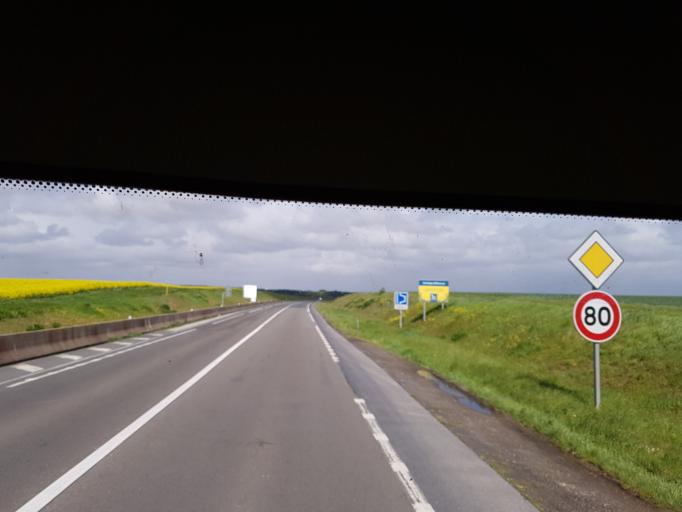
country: FR
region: Nord-Pas-de-Calais
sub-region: Departement du Nord
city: Proville
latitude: 50.1487
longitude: 3.2009
